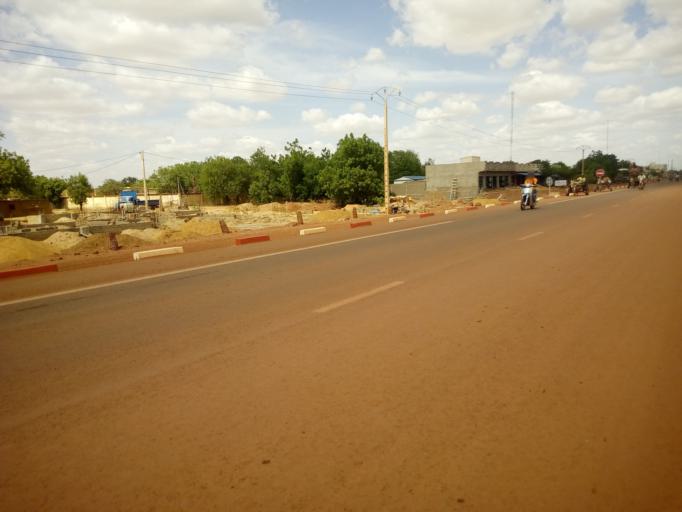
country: ML
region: Segou
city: Segou
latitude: 13.4349
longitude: -6.2327
